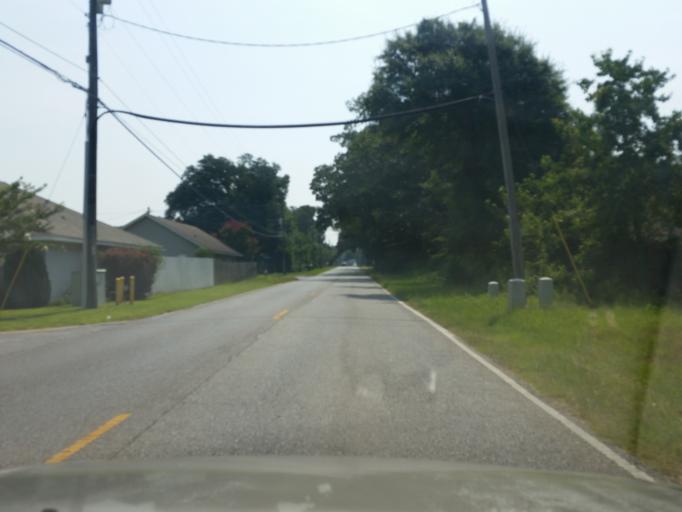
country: US
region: Florida
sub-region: Escambia County
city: Ensley
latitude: 30.5191
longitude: -87.2851
